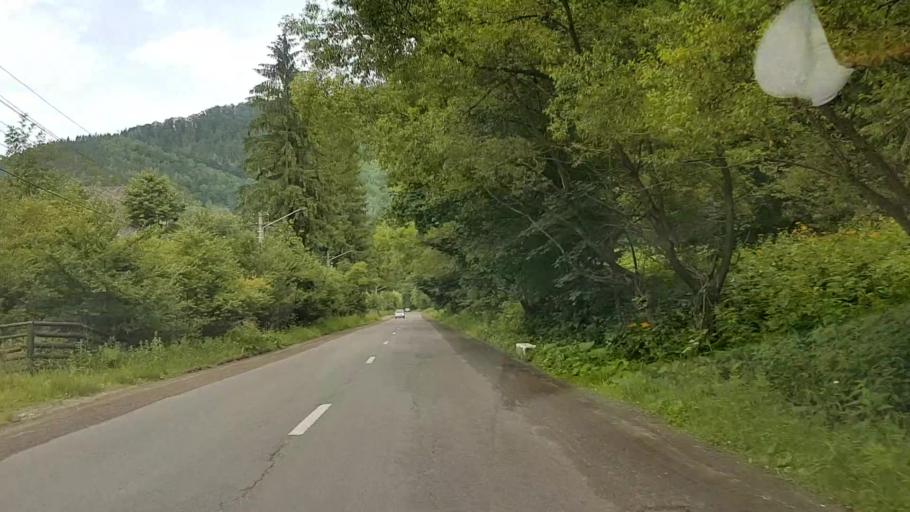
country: RO
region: Neamt
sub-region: Comuna Bicaz
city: Dodeni
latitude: 46.9373
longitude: 26.0900
